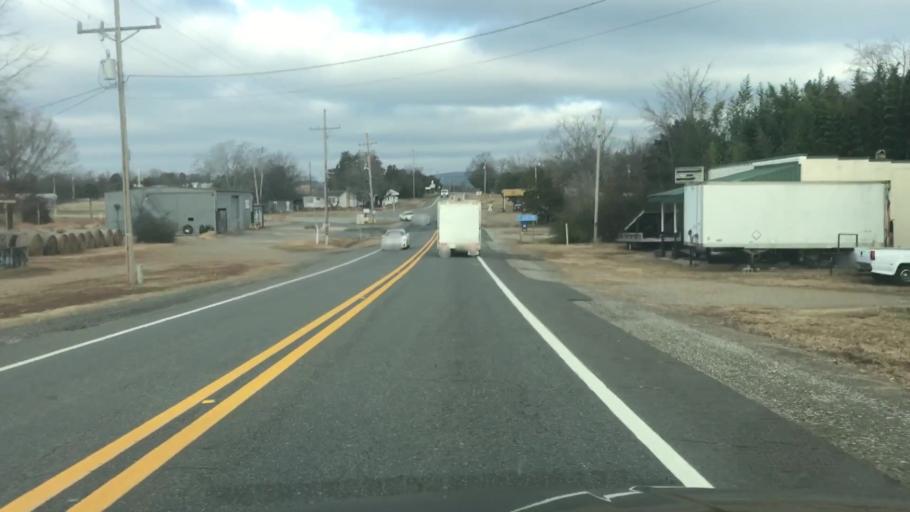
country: US
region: Arkansas
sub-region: Montgomery County
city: Mount Ida
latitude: 34.6287
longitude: -93.7331
